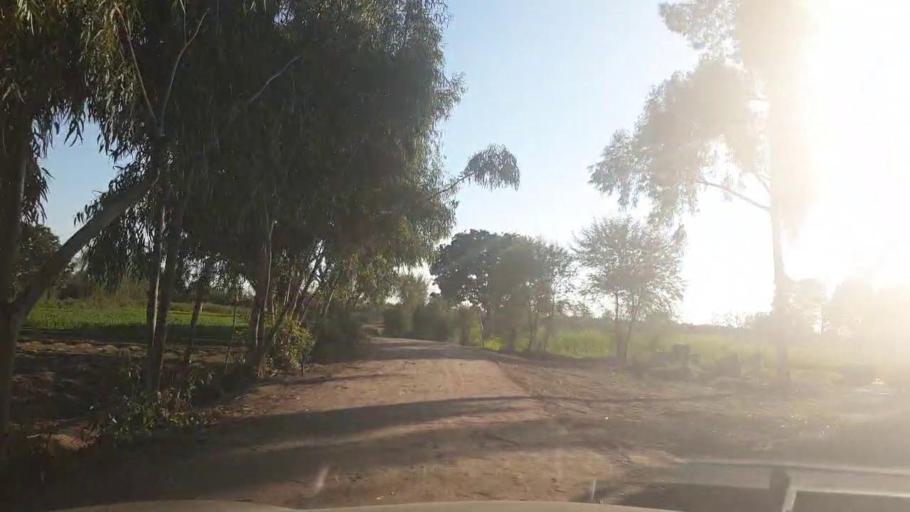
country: PK
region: Sindh
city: Ghotki
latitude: 27.9919
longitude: 69.2608
